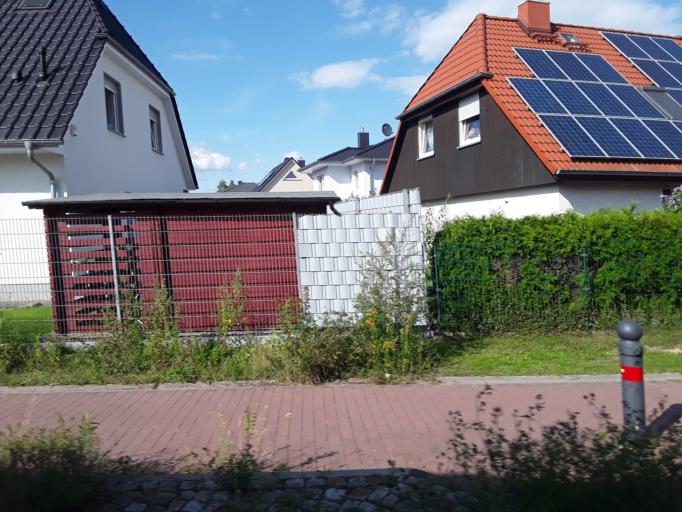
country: DE
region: Berlin
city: Buch
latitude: 52.6309
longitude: 13.5211
